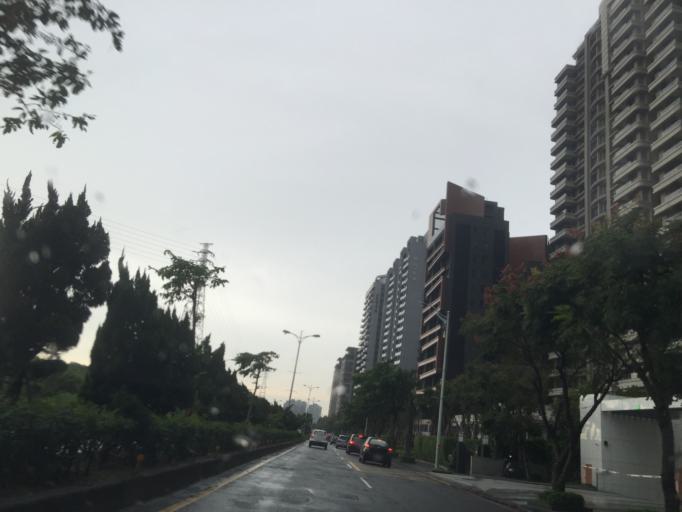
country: TW
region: Taiwan
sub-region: Hsinchu
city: Zhubei
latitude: 24.8187
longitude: 121.0101
